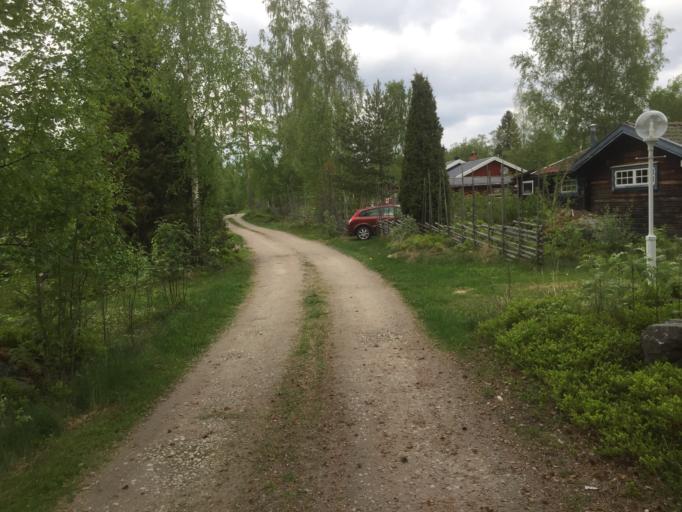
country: SE
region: Uppsala
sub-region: Alvkarleby Kommun
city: Skutskaer
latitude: 60.7906
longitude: 17.2967
